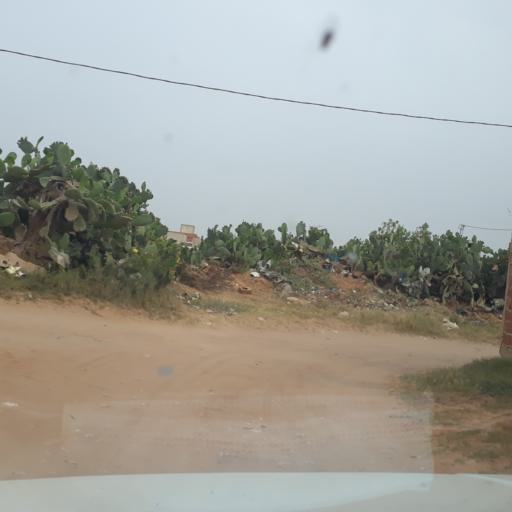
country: TN
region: Safaqis
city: Al Qarmadah
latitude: 34.8269
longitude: 10.7771
